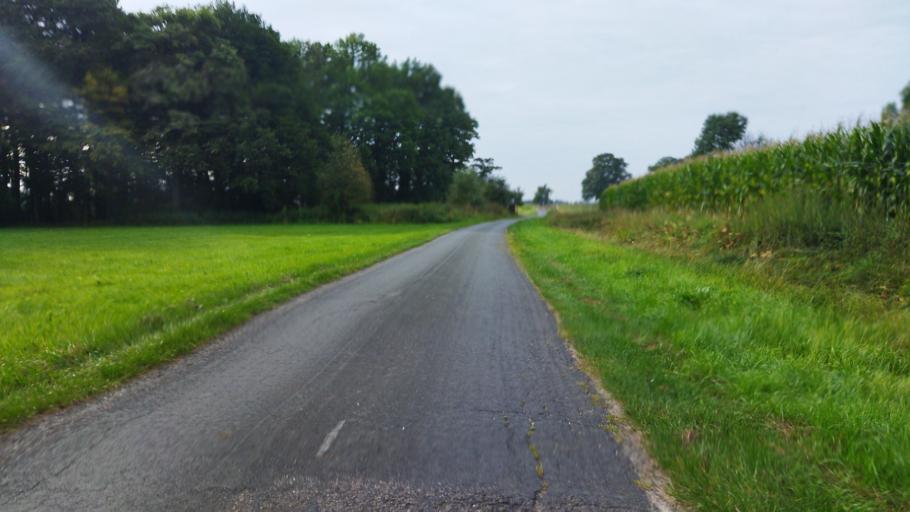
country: DE
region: Lower Saxony
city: Bad Laer
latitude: 52.0776
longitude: 8.1088
